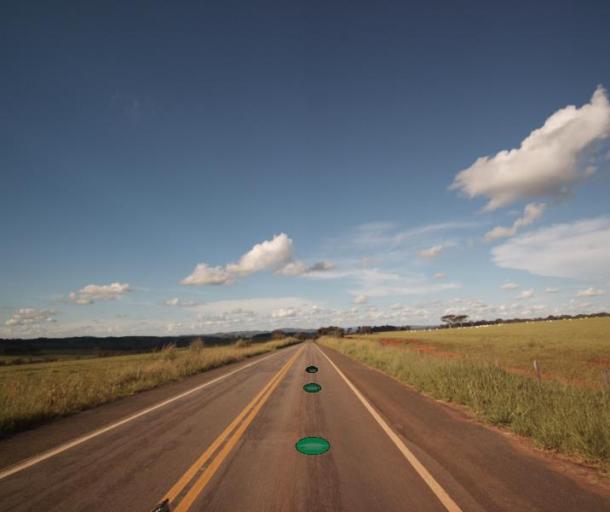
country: BR
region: Goias
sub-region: Itaberai
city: Itaberai
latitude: -15.9746
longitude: -49.6783
